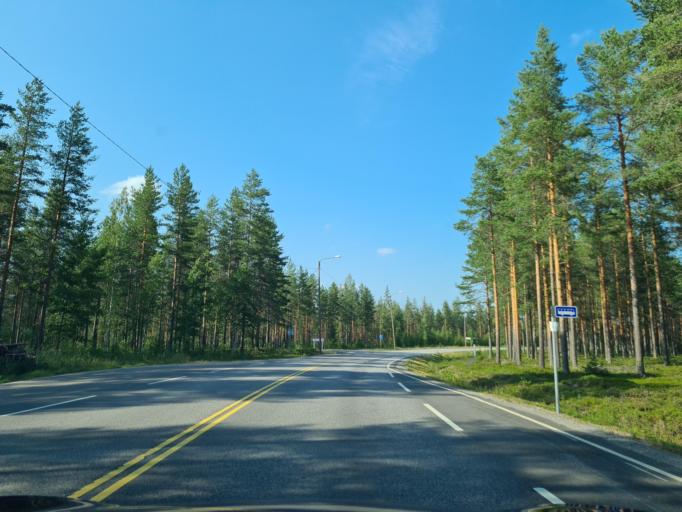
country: FI
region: Satakunta
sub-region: Pohjois-Satakunta
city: Karvia
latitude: 62.0733
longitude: 22.5065
